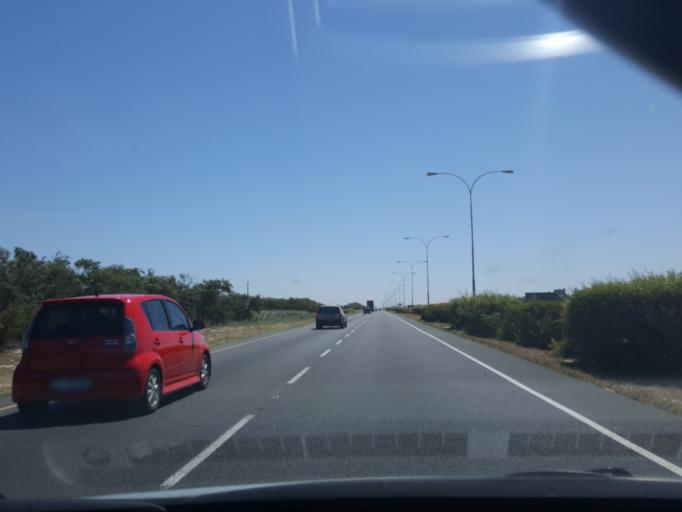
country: ZA
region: Western Cape
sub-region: City of Cape Town
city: Sunset Beach
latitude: -33.8394
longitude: 18.5361
